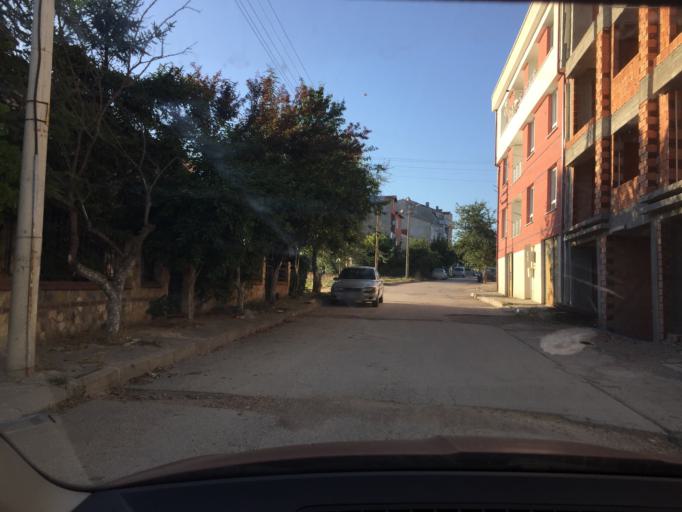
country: TR
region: Eskisehir
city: Eskisehir
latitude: 39.7754
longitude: 30.4530
